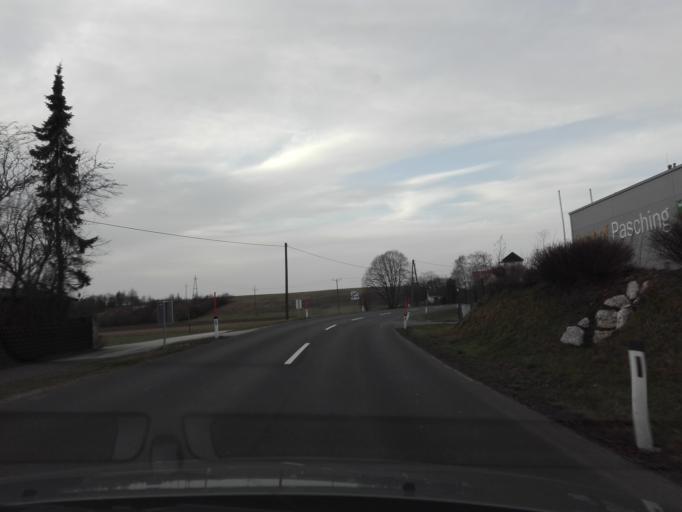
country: AT
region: Upper Austria
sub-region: Politischer Bezirk Linz-Land
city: Traun
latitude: 48.2398
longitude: 14.2274
